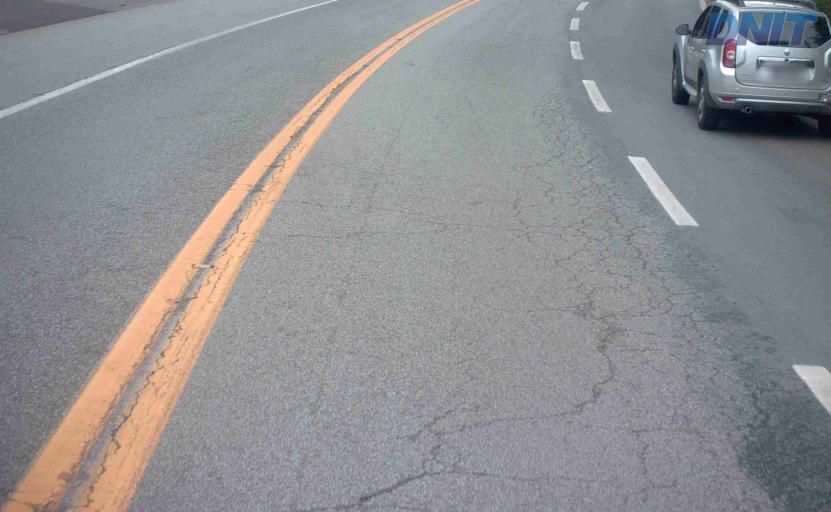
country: BR
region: Minas Gerais
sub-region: Barao De Cocais
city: Barao de Cocais
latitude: -19.7371
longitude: -43.5121
